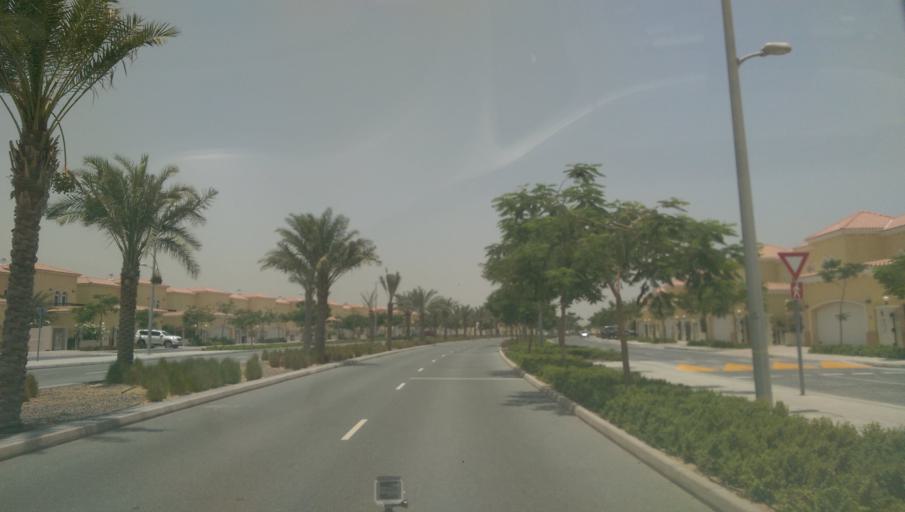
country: AE
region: Dubai
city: Dubai
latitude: 25.0385
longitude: 55.1632
